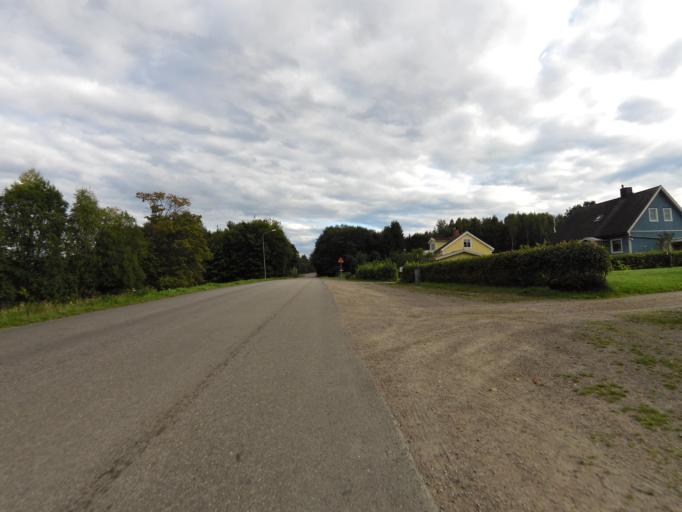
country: SE
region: Gaevleborg
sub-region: Gavle Kommun
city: Valbo
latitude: 60.6520
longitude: 17.0146
